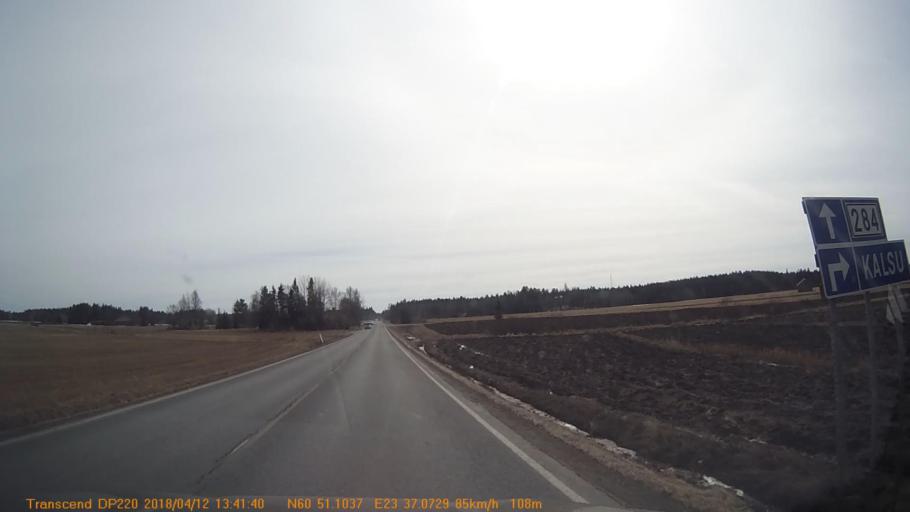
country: FI
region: Haeme
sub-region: Forssa
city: Forssa
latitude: 60.8509
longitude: 23.6179
